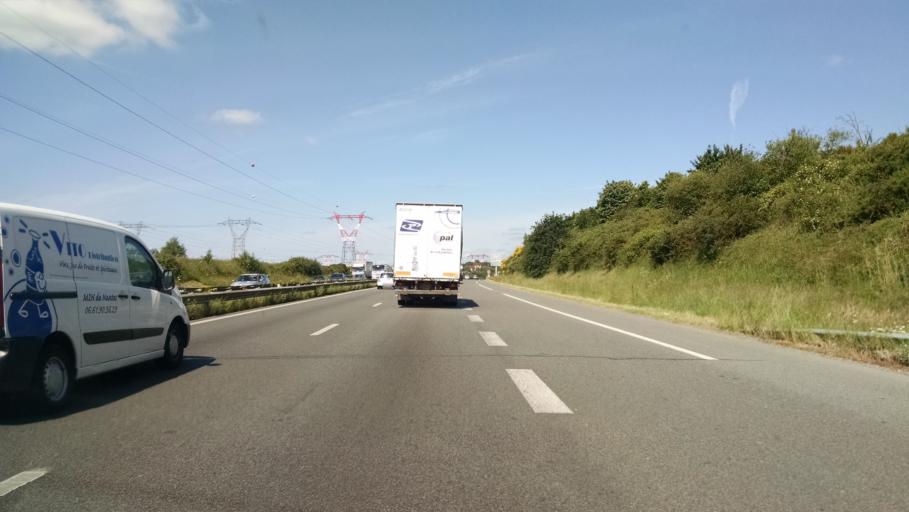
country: FR
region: Pays de la Loire
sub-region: Departement de la Loire-Atlantique
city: Reze
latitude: 47.1702
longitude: -1.5840
